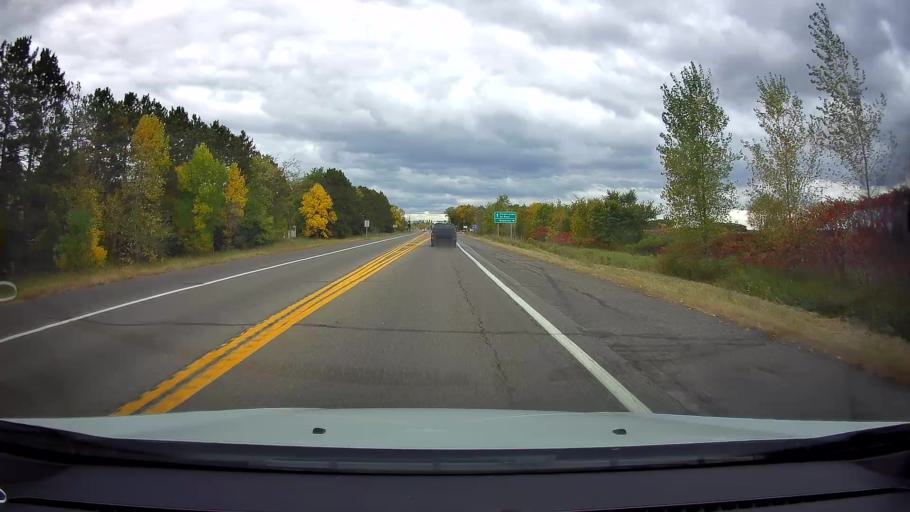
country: US
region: Minnesota
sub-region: Chisago County
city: Chisago City
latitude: 45.3590
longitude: -92.9087
